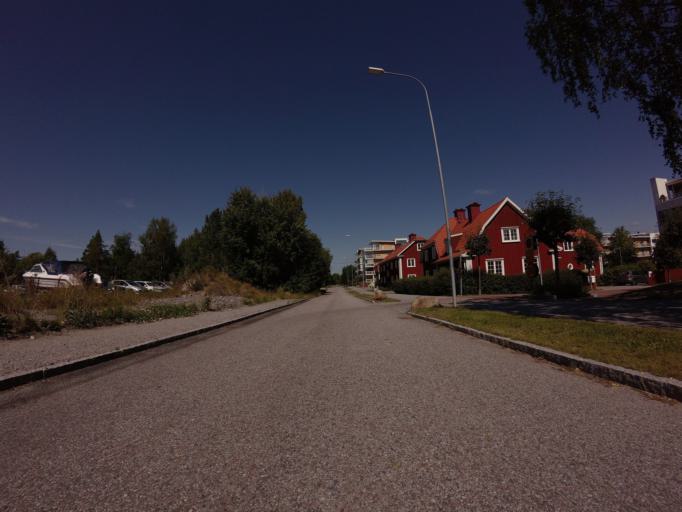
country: SE
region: Stockholm
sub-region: Lidingo
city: Brevik
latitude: 59.3576
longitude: 18.2291
